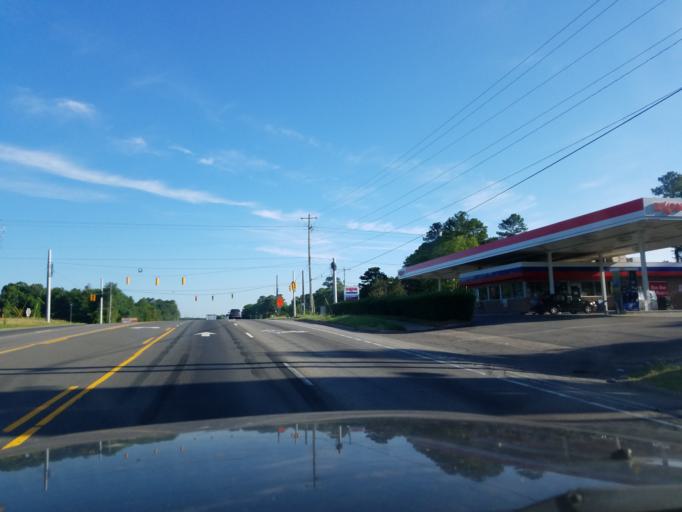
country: US
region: North Carolina
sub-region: Durham County
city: Durham
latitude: 35.9649
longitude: -78.8464
